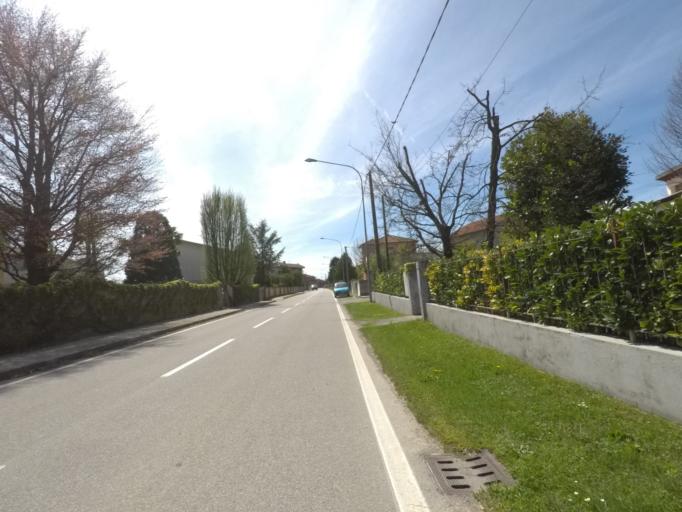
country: IT
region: Friuli Venezia Giulia
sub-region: Provincia di Pordenone
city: Casarsa della Delizia
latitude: 45.9432
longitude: 12.8444
